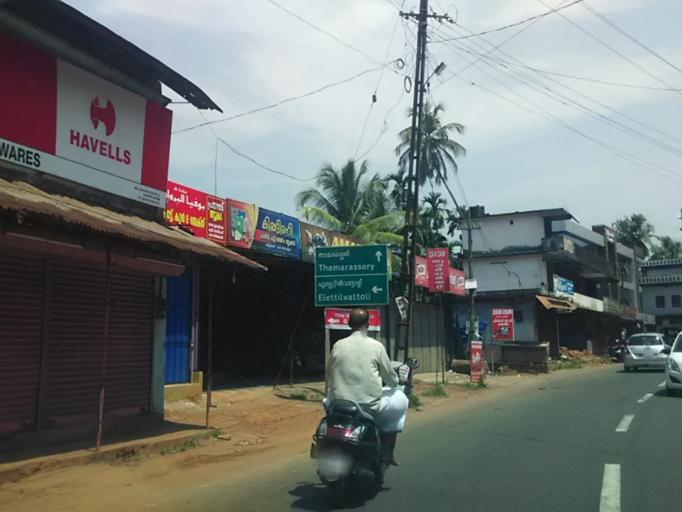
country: IN
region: Kerala
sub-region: Kozhikode
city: Kunnamangalam
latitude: 11.3775
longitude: 75.9105
